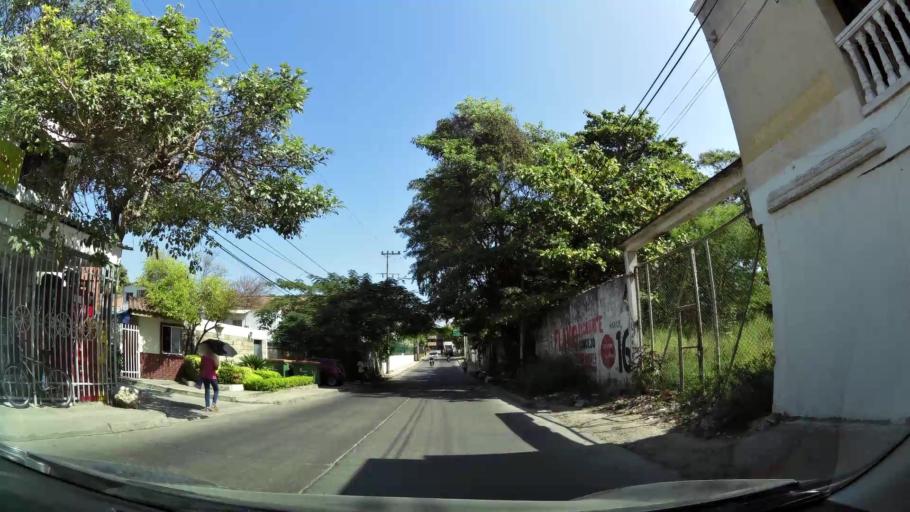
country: CO
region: Bolivar
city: Cartagena
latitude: 10.3847
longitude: -75.4720
